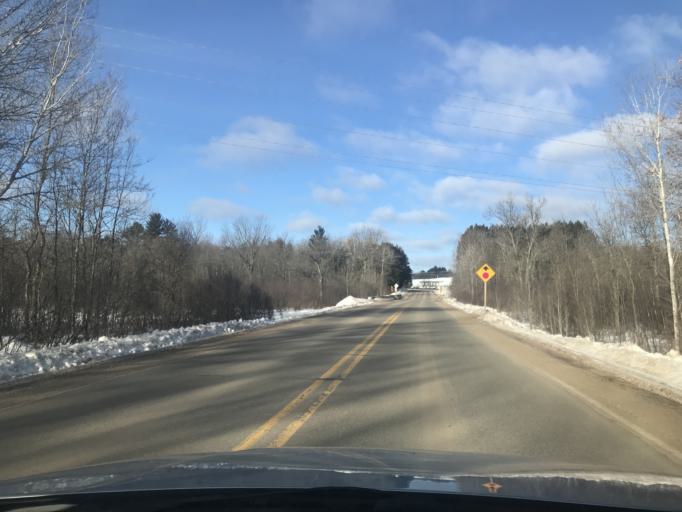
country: US
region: Wisconsin
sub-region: Marinette County
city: Niagara
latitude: 45.6383
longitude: -87.9757
